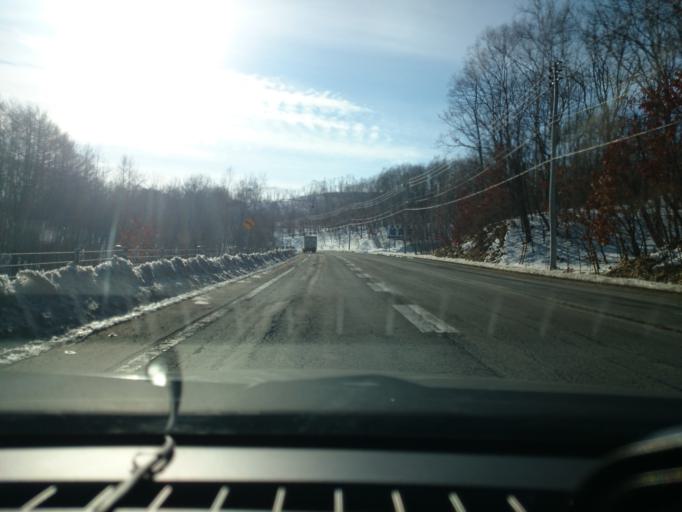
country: JP
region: Hokkaido
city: Otofuke
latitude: 43.2334
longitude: 143.5266
